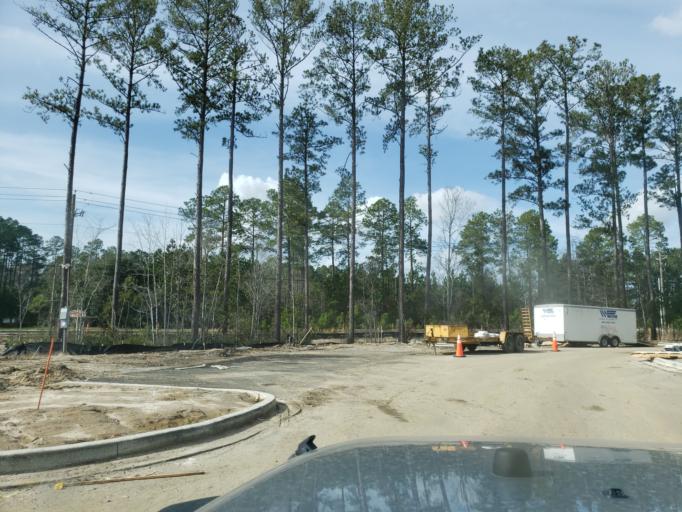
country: US
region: Georgia
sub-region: Chatham County
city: Pooler
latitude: 32.1712
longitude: -81.2330
